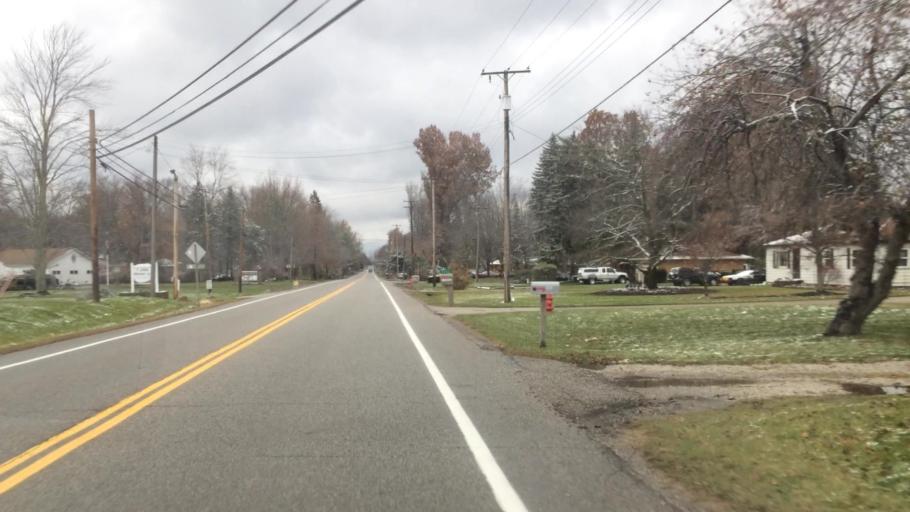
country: US
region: Ohio
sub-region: Summit County
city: Macedonia
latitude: 41.2956
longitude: -81.5239
